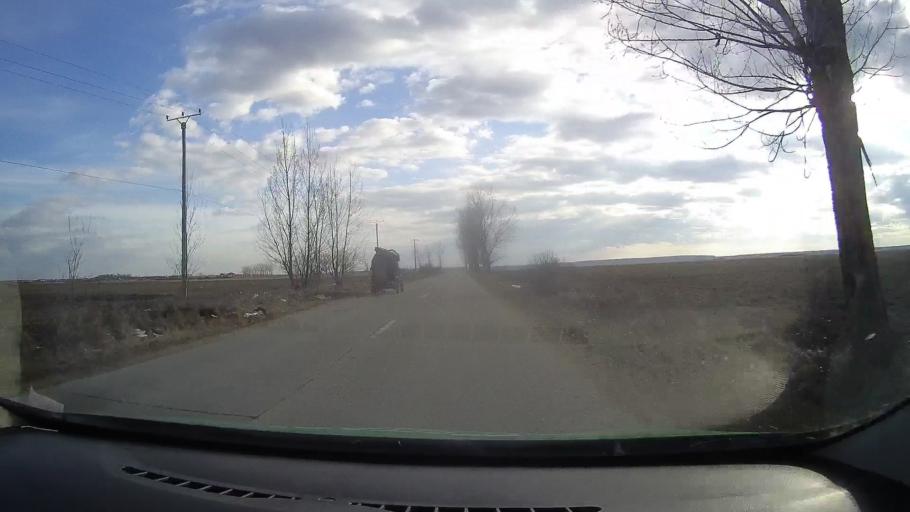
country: RO
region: Dambovita
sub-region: Comuna Vacaresti
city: Vacaresti
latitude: 44.8778
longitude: 25.4633
